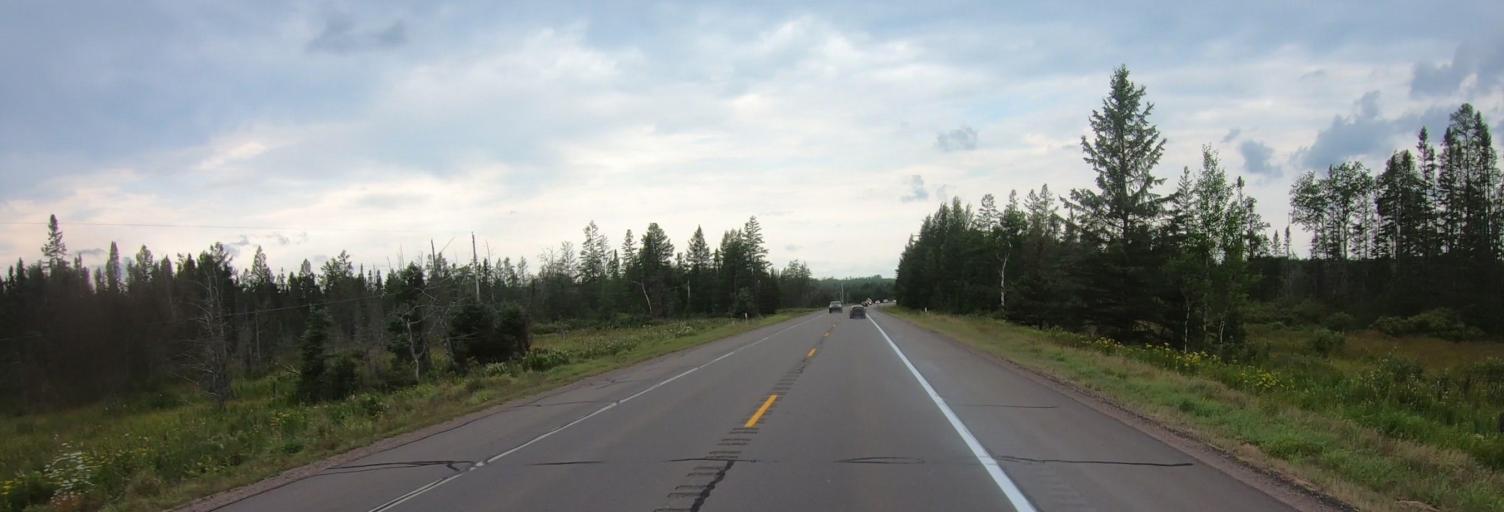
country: US
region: Michigan
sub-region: Marquette County
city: West Ishpeming
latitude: 46.4913
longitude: -87.8449
